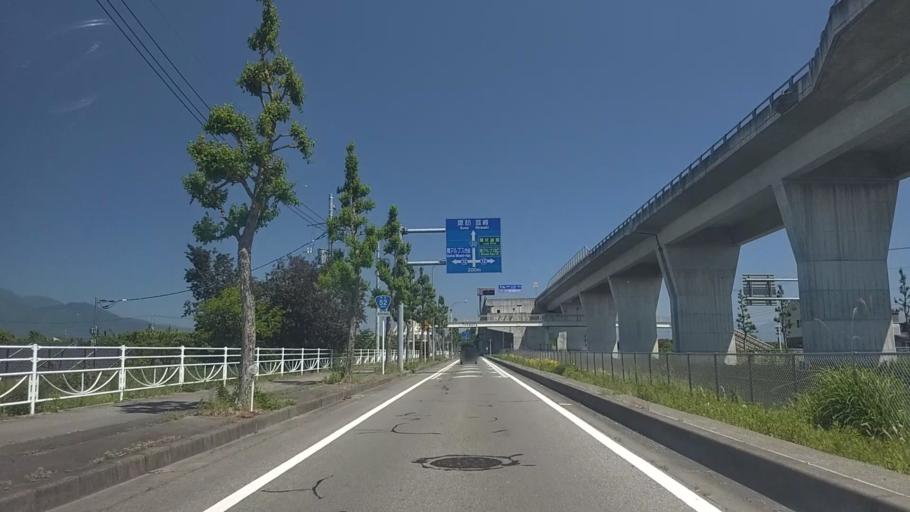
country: JP
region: Yamanashi
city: Ryuo
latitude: 35.6104
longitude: 138.4808
